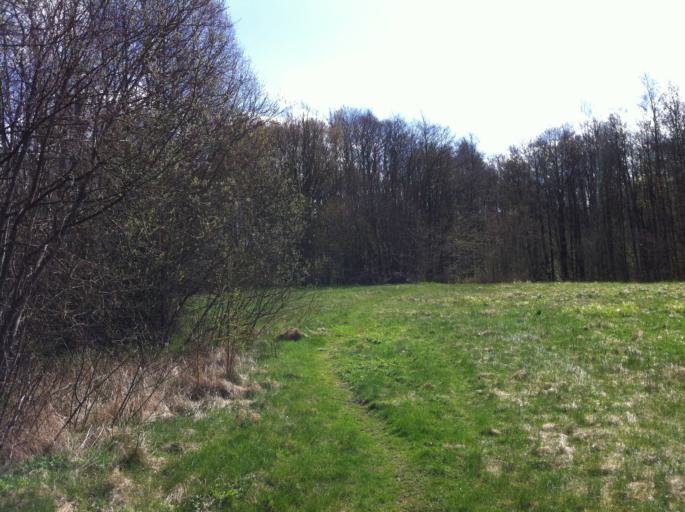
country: SE
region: Skane
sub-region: Horby Kommun
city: Hoerby
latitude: 55.9193
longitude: 13.6308
